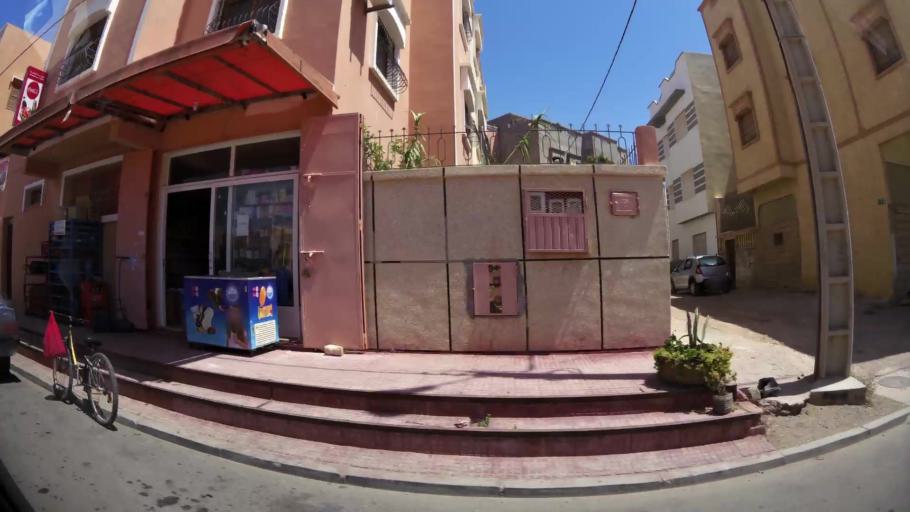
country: MA
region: Souss-Massa-Draa
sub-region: Inezgane-Ait Mellou
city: Inezgane
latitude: 30.3499
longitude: -9.4844
